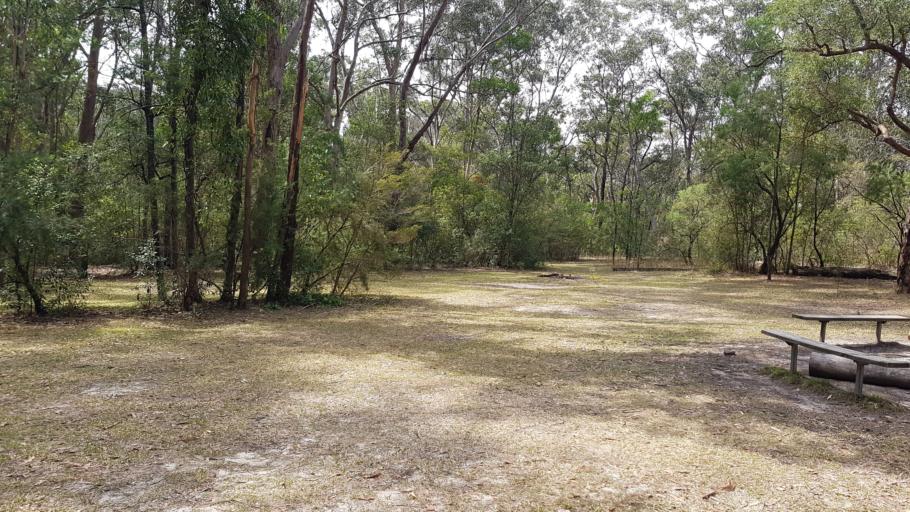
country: AU
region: New South Wales
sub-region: Gosford Shire
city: Point Clare
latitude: -33.3275
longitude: 151.0896
